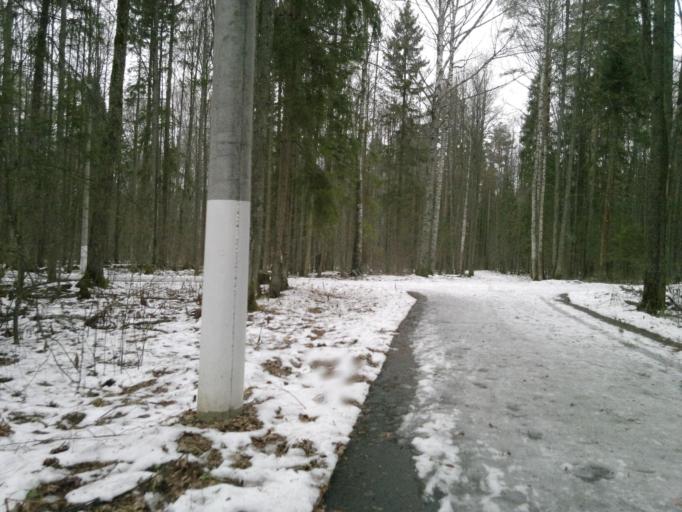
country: RU
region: Mariy-El
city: Yoshkar-Ola
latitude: 56.6029
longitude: 47.9643
